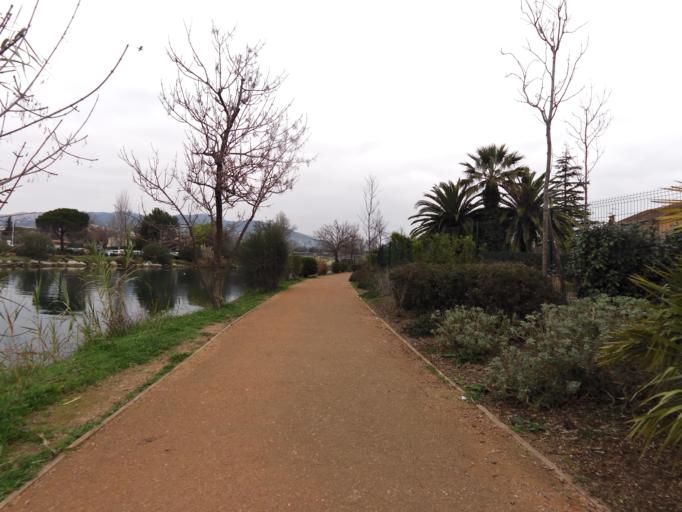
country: FR
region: Provence-Alpes-Cote d'Azur
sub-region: Departement des Alpes-Maritimes
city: Mandelieu-la-Napoule
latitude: 43.5344
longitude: 6.9446
